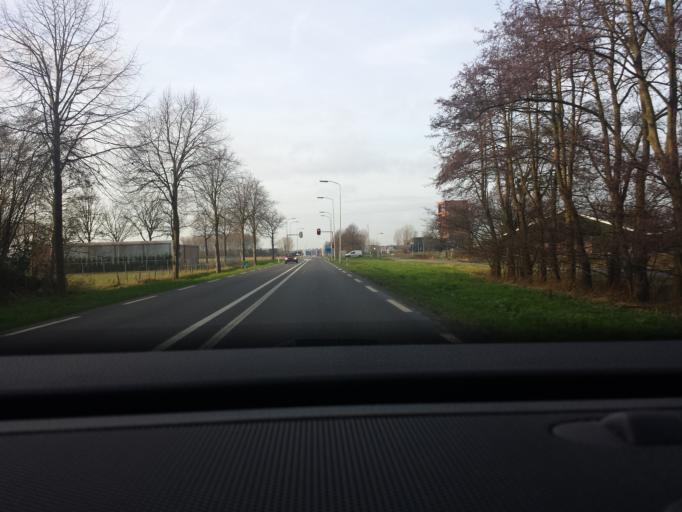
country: NL
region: Gelderland
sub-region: Gemeente Duiven
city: Duiven
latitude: 51.9555
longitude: 6.0296
